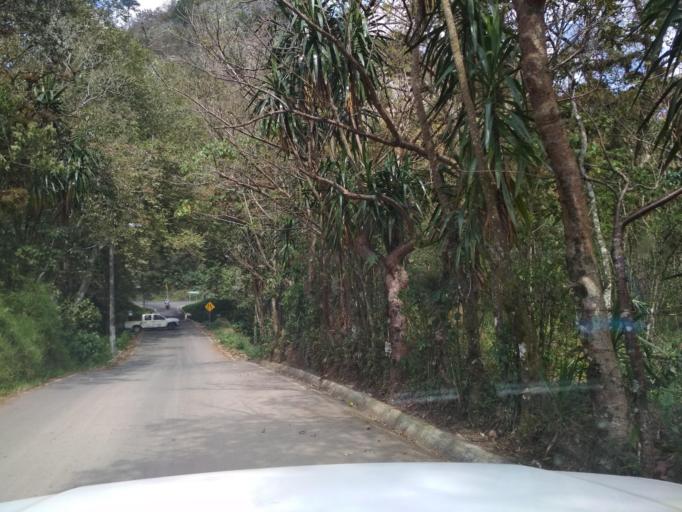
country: MX
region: Veracruz
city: Jalapilla
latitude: 18.7940
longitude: -97.1027
